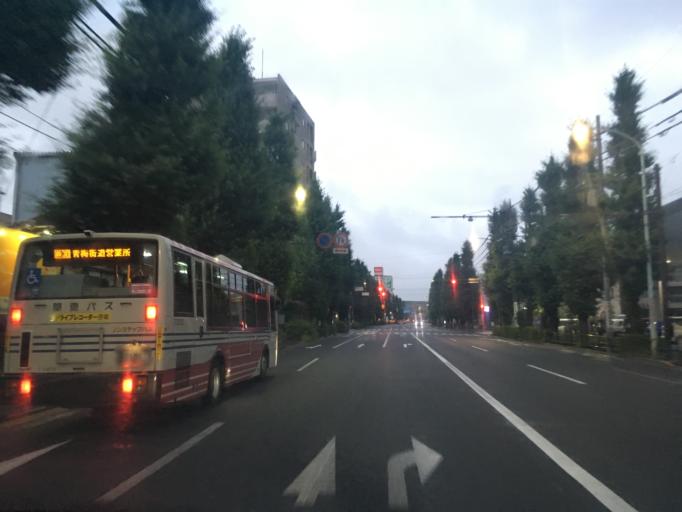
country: JP
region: Tokyo
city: Musashino
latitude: 35.7138
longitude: 139.5993
